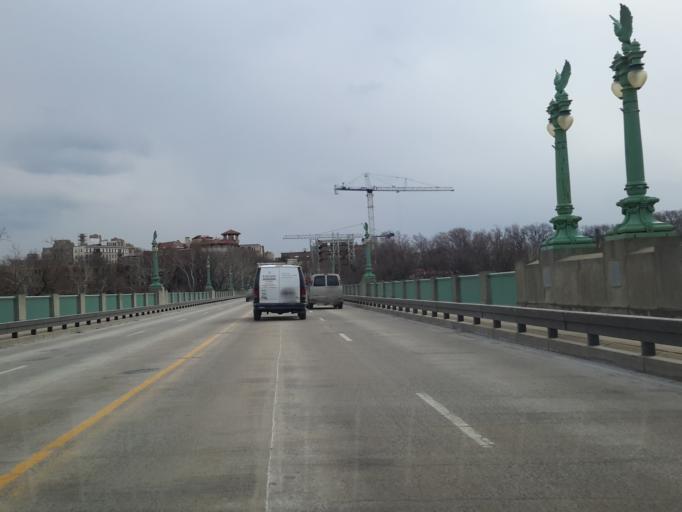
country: US
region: Washington, D.C.
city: Washington, D.C.
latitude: 38.9225
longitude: -77.0508
